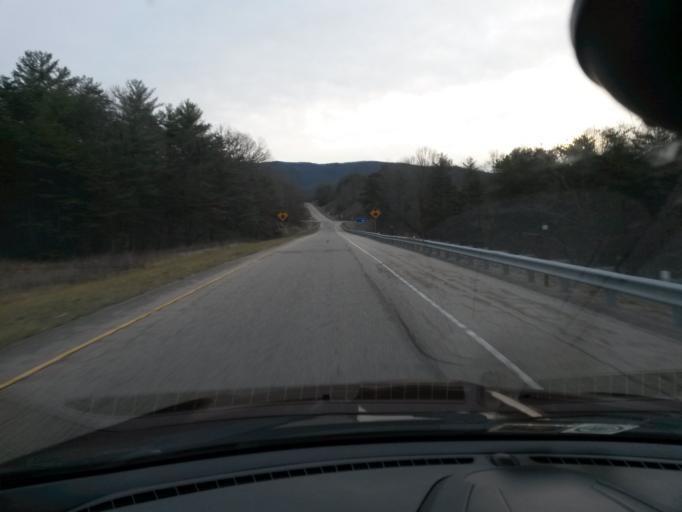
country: US
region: Virginia
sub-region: Alleghany County
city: Clifton Forge
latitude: 37.8309
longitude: -79.7650
